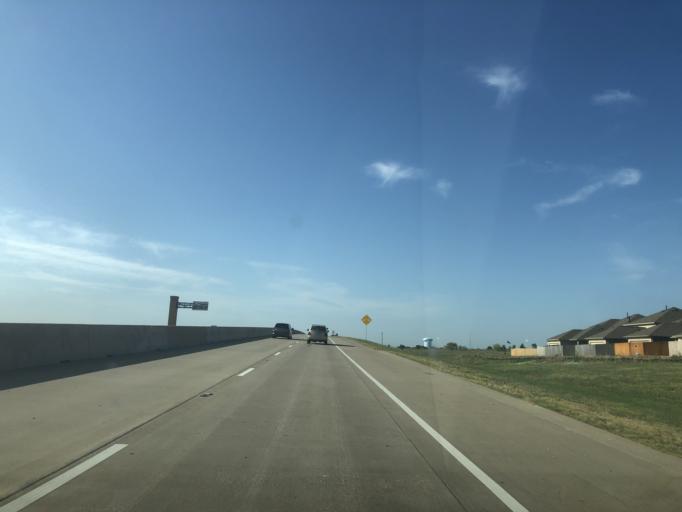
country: US
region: Texas
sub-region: Tarrant County
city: Crowley
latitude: 32.6185
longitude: -97.4127
